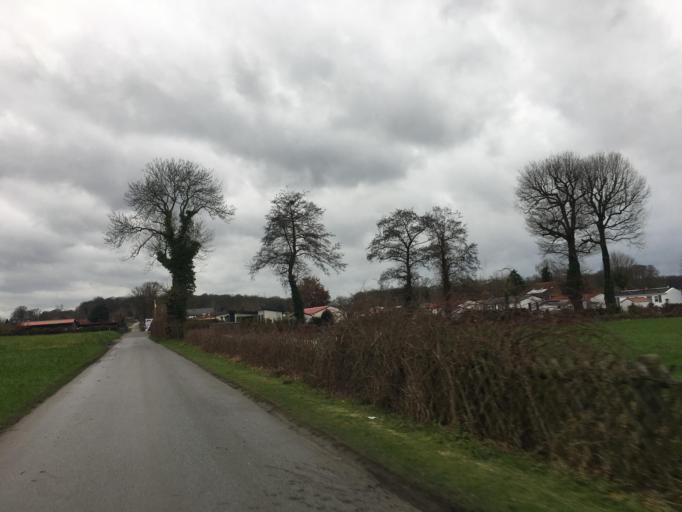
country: DE
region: North Rhine-Westphalia
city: Oer-Erkenschwick
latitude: 51.6819
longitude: 7.3078
